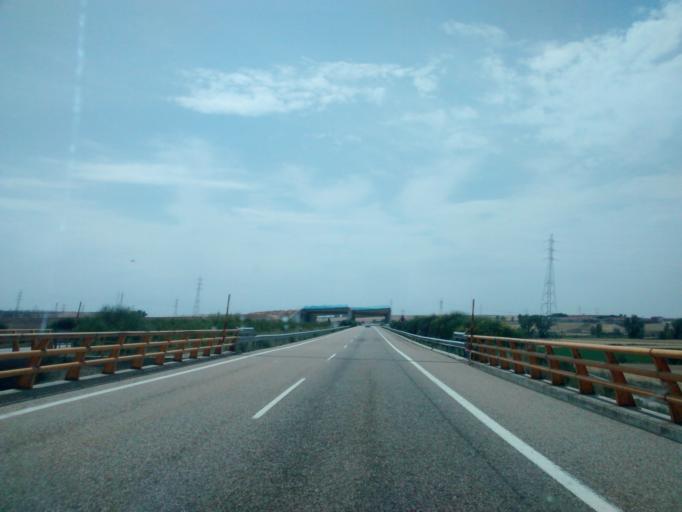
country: ES
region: Castille and Leon
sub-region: Provincia de Burgos
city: San Mames de Burgos
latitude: 42.3484
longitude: -3.7940
